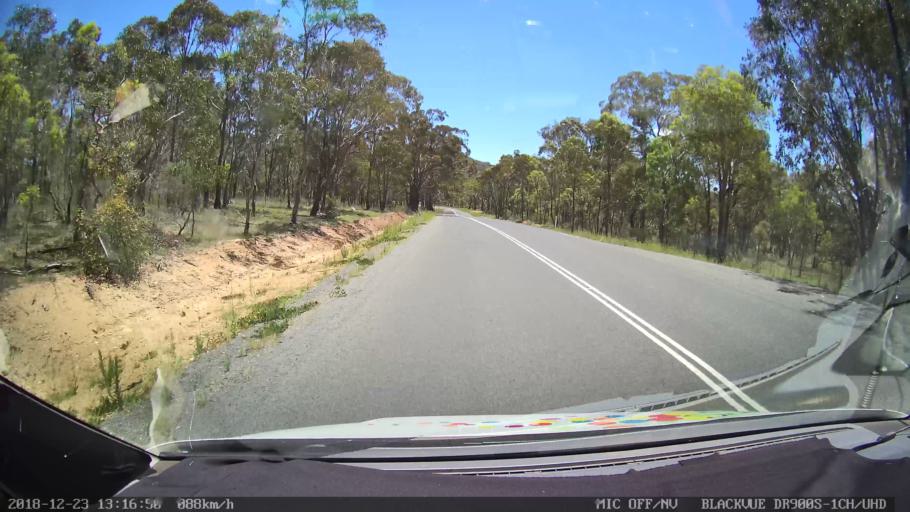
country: AU
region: New South Wales
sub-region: Armidale Dumaresq
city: Armidale
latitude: -30.4957
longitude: 151.4962
